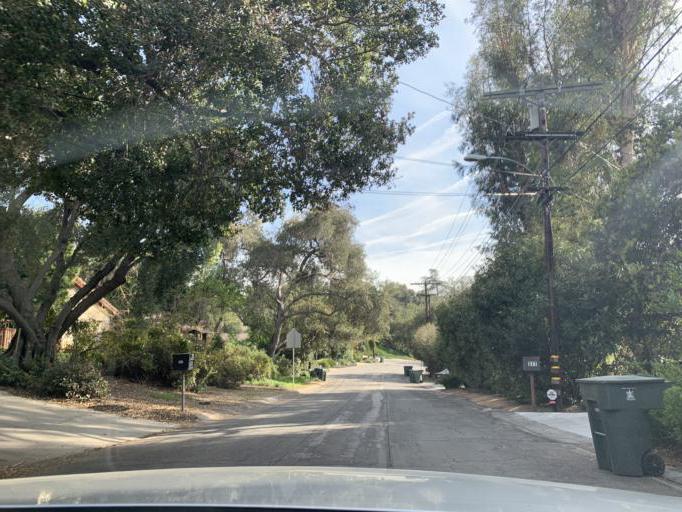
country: US
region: California
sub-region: Los Angeles County
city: South Pasadena
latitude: 34.1354
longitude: -118.1731
